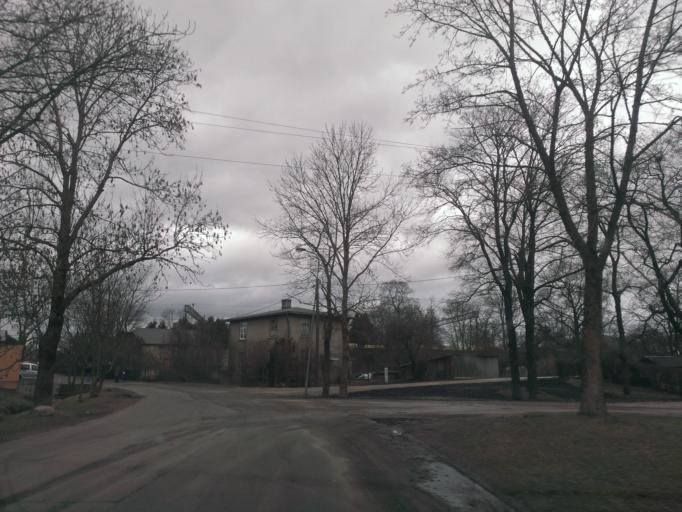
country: LV
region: Salaspils
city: Salaspils
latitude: 56.8596
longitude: 24.3500
